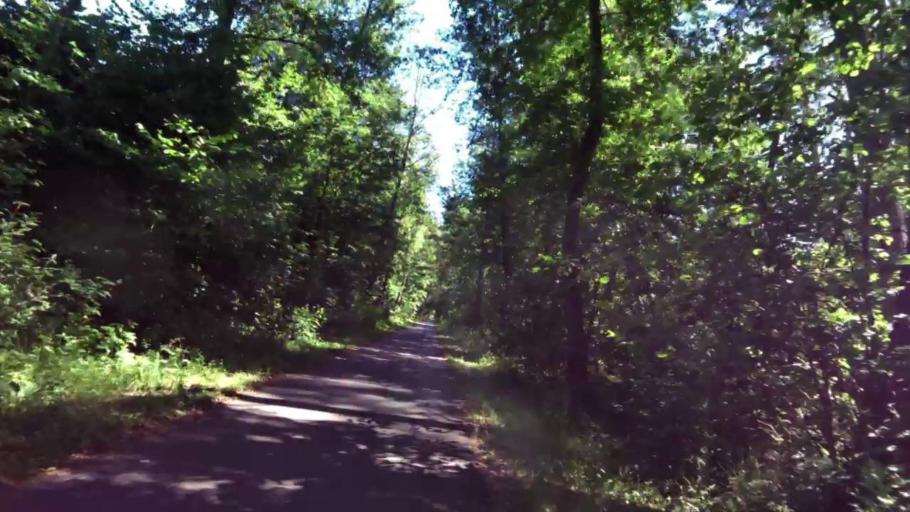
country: PL
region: West Pomeranian Voivodeship
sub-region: Powiat bialogardzki
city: Karlino
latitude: 54.0540
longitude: 15.8754
